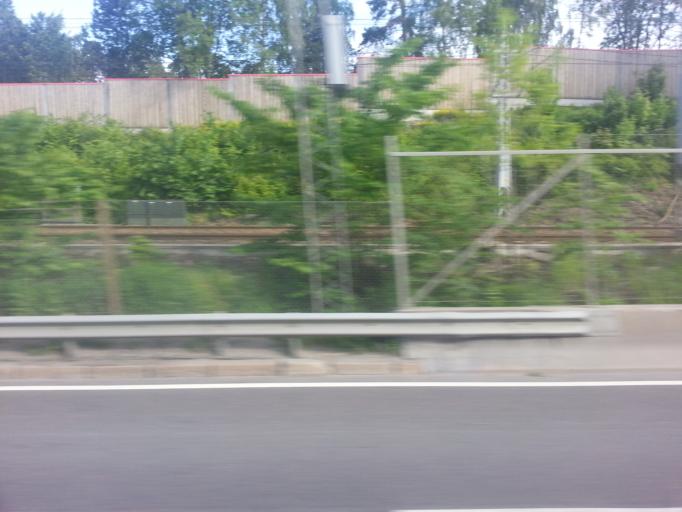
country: NO
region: Akershus
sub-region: Baerum
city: Lysaker
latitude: 59.9147
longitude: 10.6472
